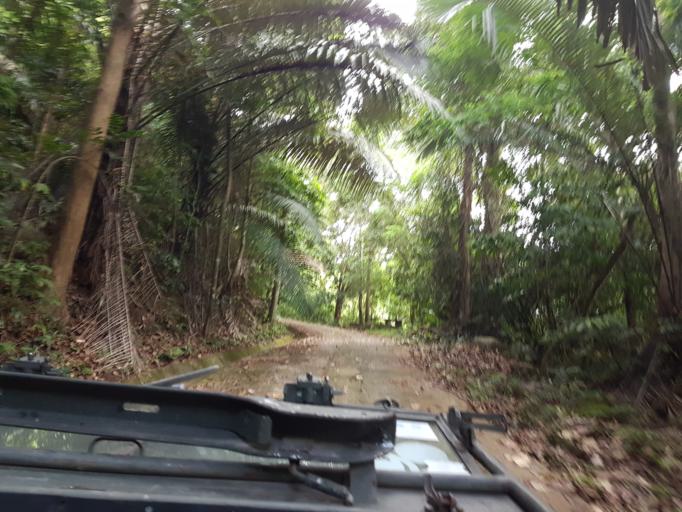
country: TH
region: Pattani
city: Khok Pho
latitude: 6.6561
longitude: 101.0988
